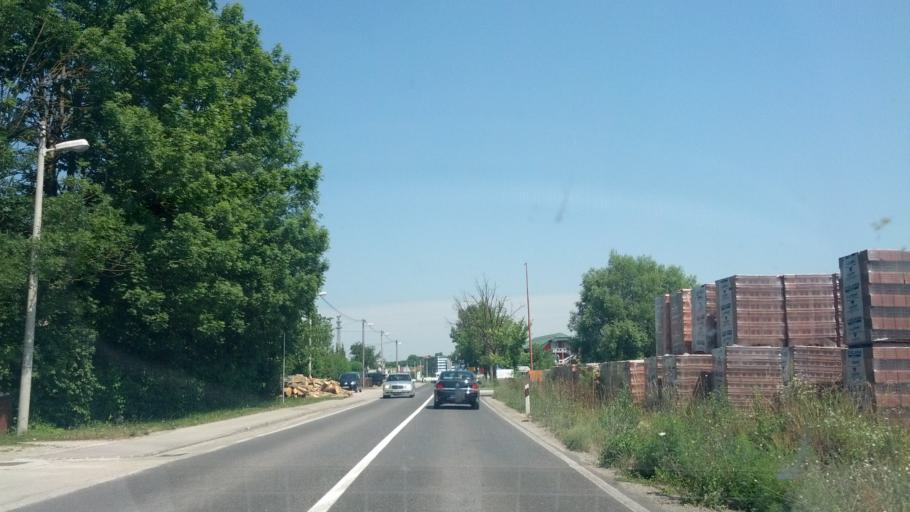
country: BA
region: Federation of Bosnia and Herzegovina
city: Bihac
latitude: 44.8320
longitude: 15.8325
